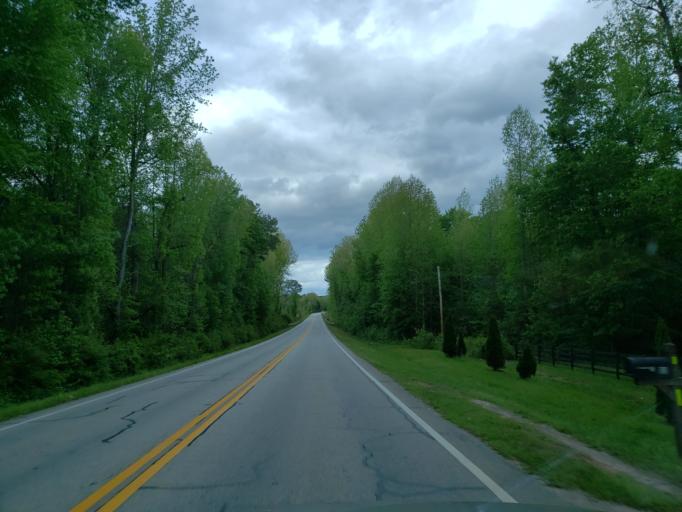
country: US
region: Georgia
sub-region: Carroll County
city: Temple
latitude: 33.8245
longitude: -85.0713
